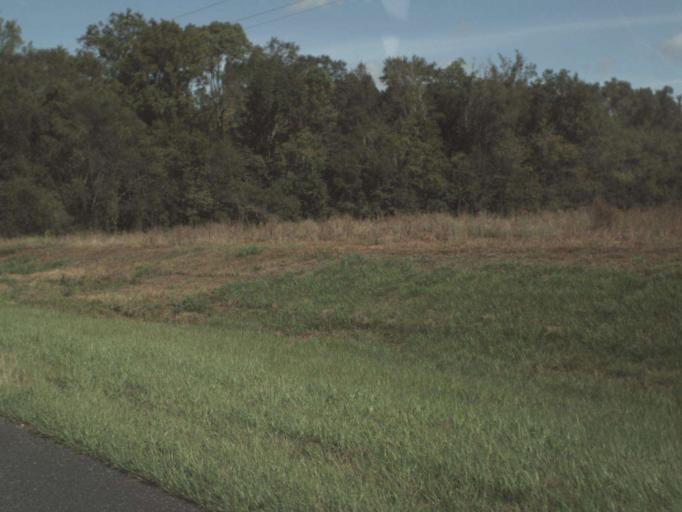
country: US
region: Florida
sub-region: Jackson County
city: Marianna
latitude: 30.8525
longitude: -85.3505
